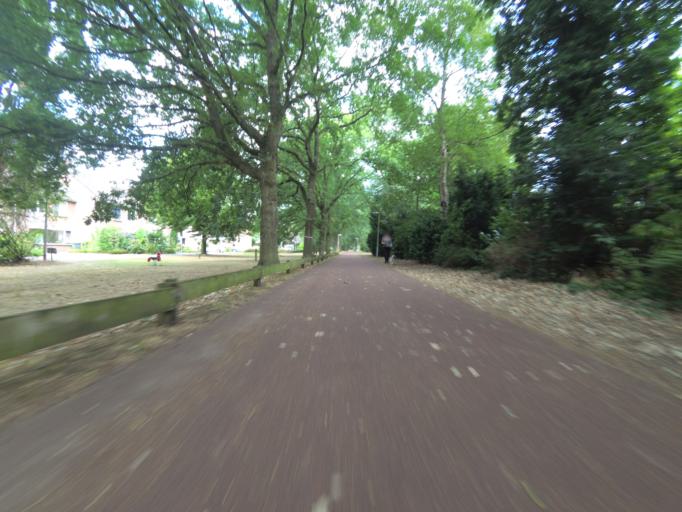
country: NL
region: Overijssel
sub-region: Gemeente Hengelo
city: Hengelo
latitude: 52.2818
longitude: 6.8406
